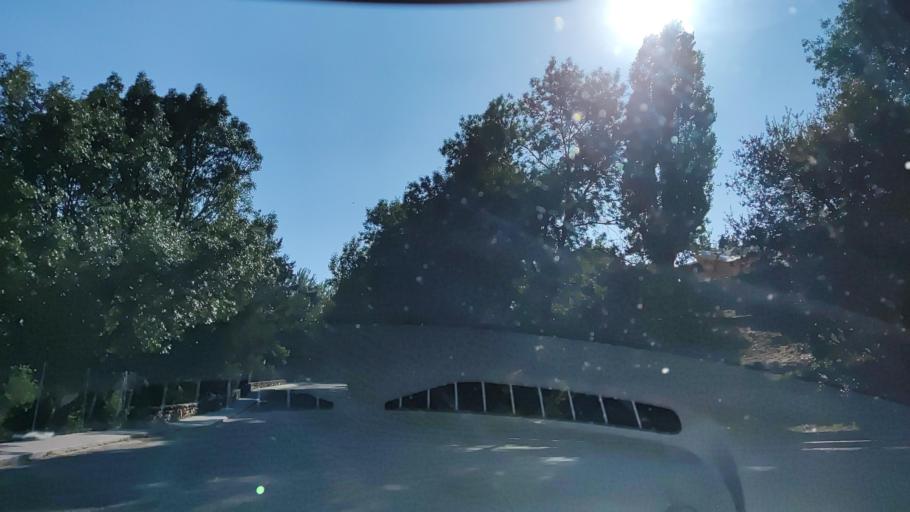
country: ES
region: Madrid
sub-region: Provincia de Madrid
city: Rascafria
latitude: 40.9014
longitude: -3.8792
